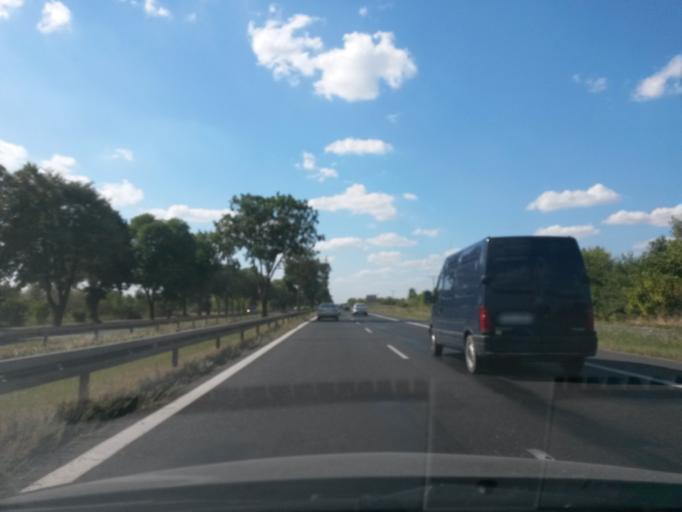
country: PL
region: Masovian Voivodeship
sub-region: Powiat warszawski zachodni
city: Truskaw
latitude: 52.3774
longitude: 20.7736
